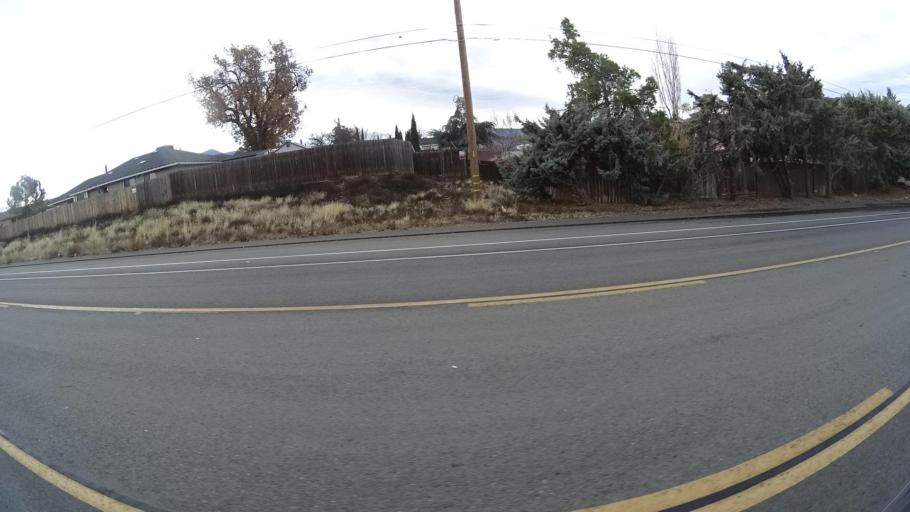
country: US
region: California
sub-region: Kern County
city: Golden Hills
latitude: 35.1451
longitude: -118.4855
